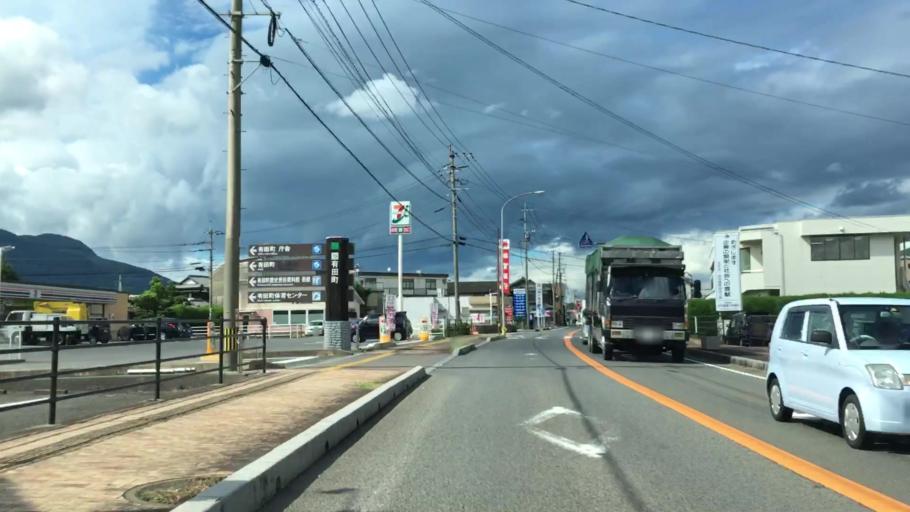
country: JP
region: Saga Prefecture
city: Imaricho-ko
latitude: 33.2114
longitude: 129.8497
